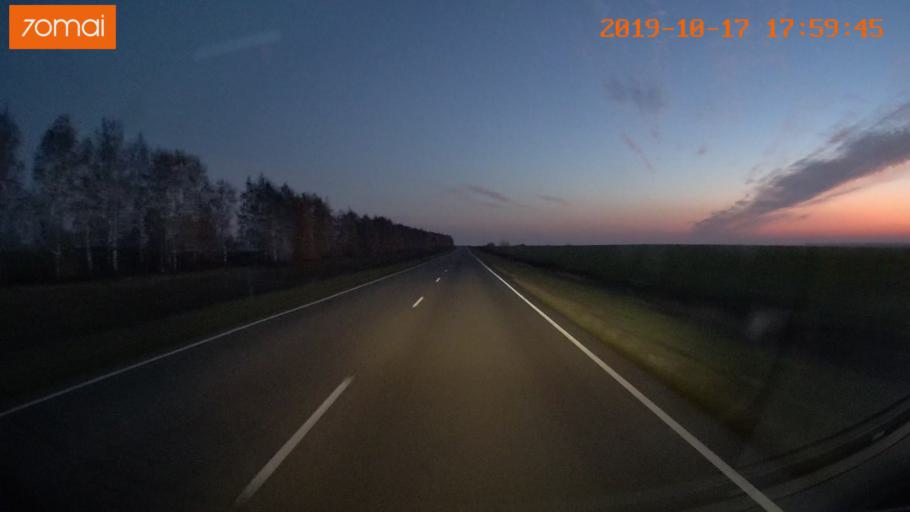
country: RU
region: Tula
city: Kurkino
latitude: 53.5322
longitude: 38.6198
